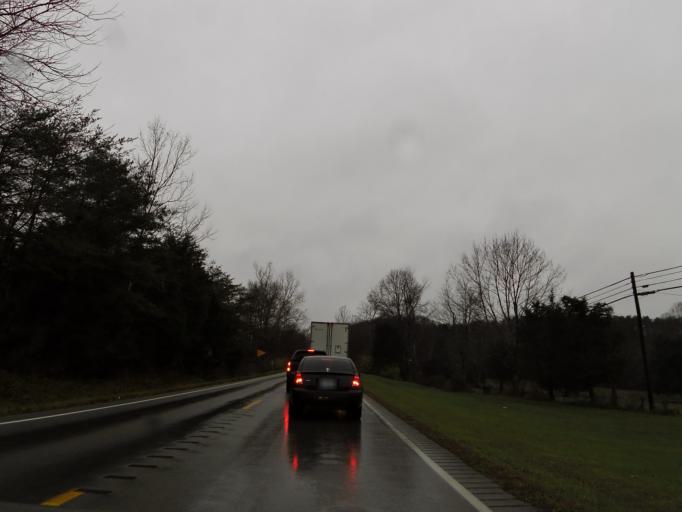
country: US
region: Kentucky
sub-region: Rockcastle County
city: Mount Vernon
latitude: 37.4233
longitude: -84.3335
